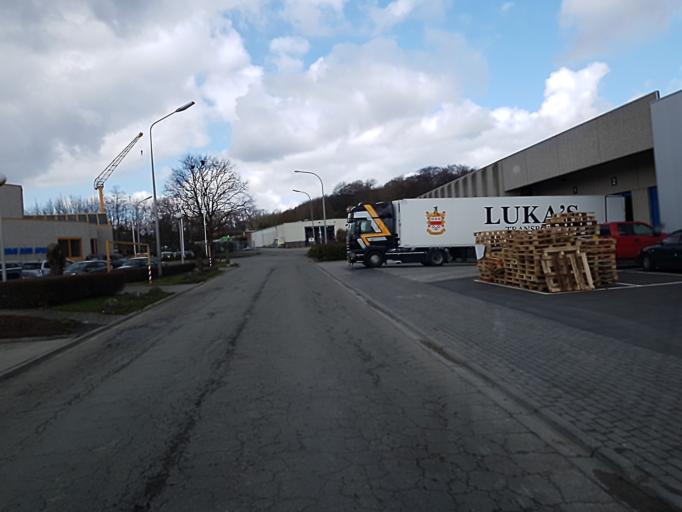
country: BE
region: Flanders
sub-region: Provincie Vlaams-Brabant
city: Ternat
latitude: 50.8885
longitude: 4.1764
